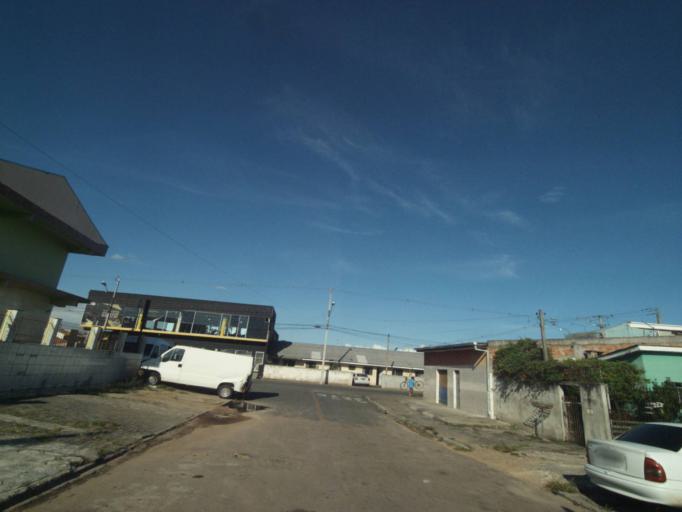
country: BR
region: Parana
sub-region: Pinhais
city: Pinhais
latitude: -25.4535
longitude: -49.2034
